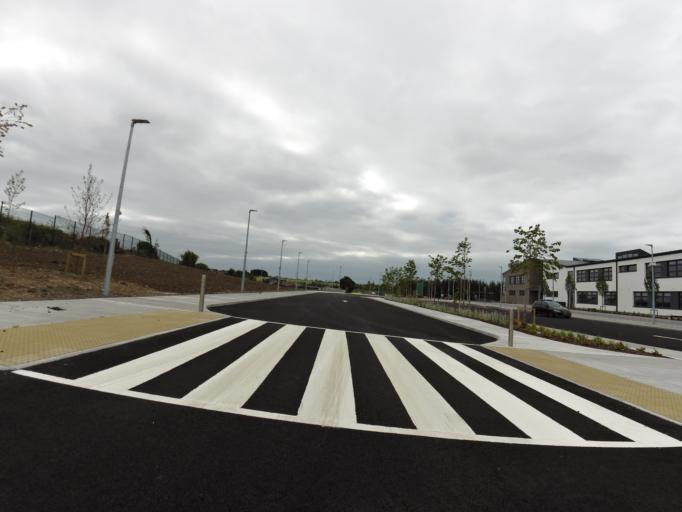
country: IE
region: Connaught
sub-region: County Galway
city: Athenry
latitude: 53.2936
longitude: -8.7541
